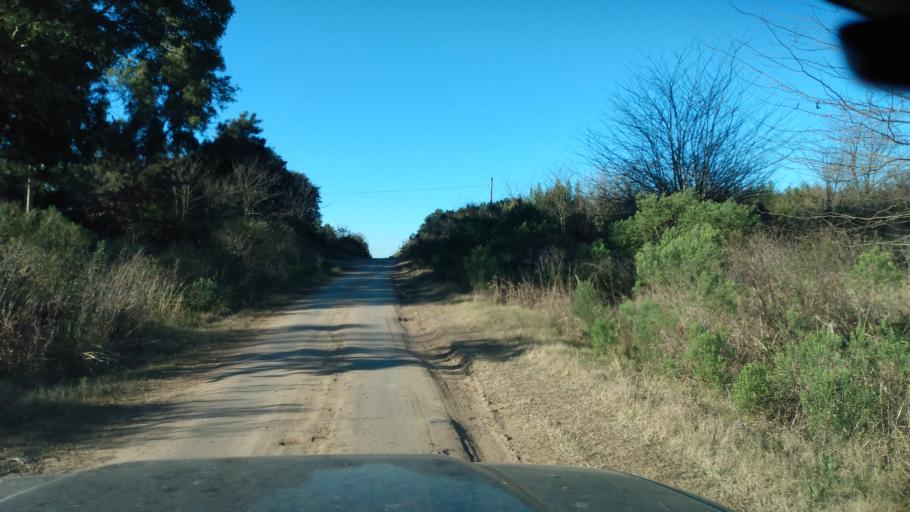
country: AR
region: Buenos Aires
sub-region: Partido de Lujan
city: Lujan
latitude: -34.5570
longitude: -59.1541
